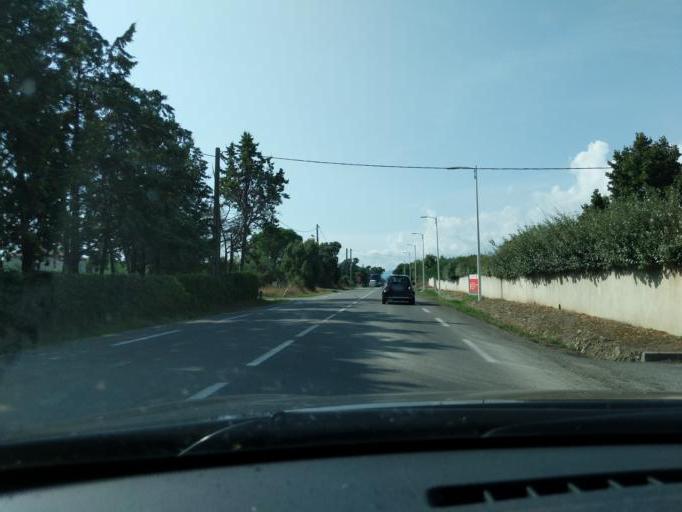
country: FR
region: Corsica
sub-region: Departement de la Haute-Corse
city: Ghisonaccia
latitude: 41.9588
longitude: 9.3965
